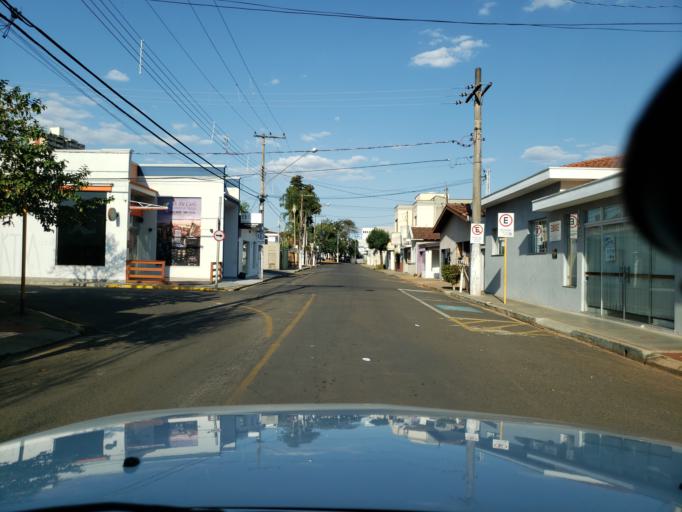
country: BR
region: Sao Paulo
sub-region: Moji-Guacu
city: Mogi-Gaucu
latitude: -22.3691
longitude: -46.9422
